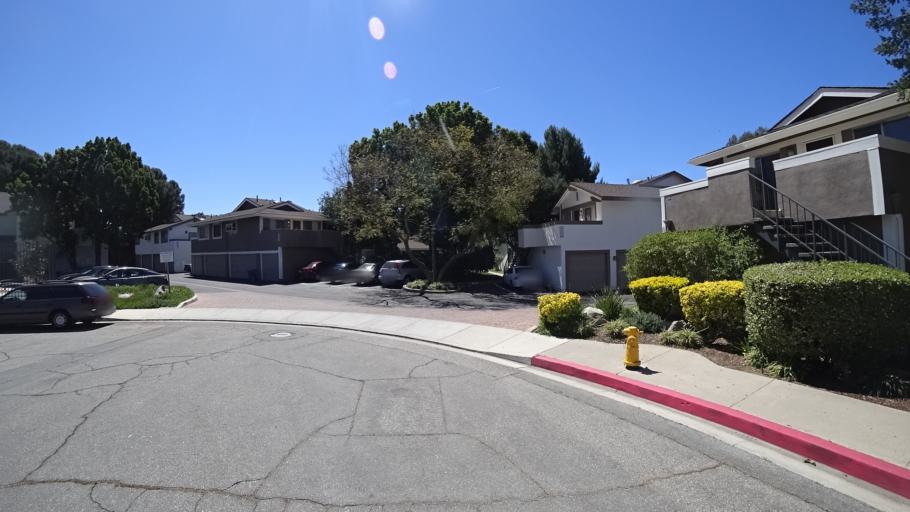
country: US
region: California
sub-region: Ventura County
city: Thousand Oaks
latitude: 34.1810
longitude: -118.8561
